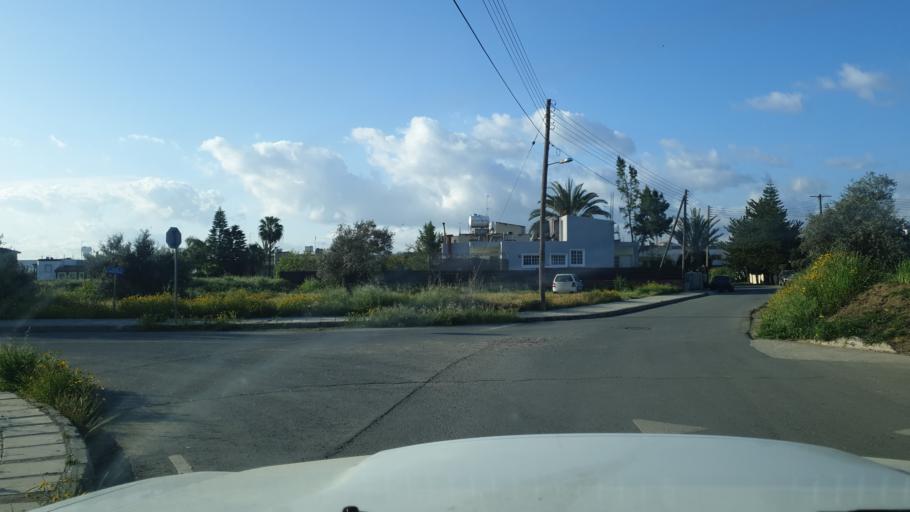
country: CY
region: Lefkosia
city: Tseri
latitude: 35.0672
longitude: 33.3271
